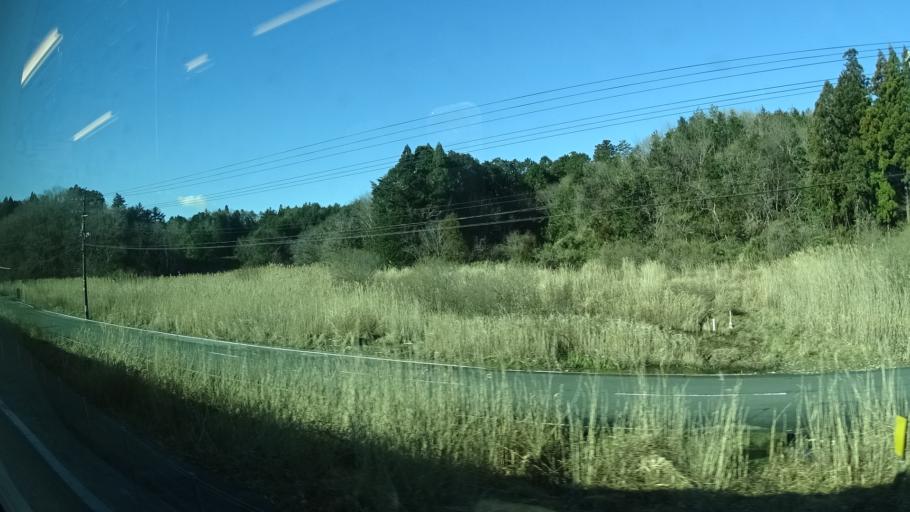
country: JP
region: Fukushima
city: Namie
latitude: 37.4625
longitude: 141.0089
